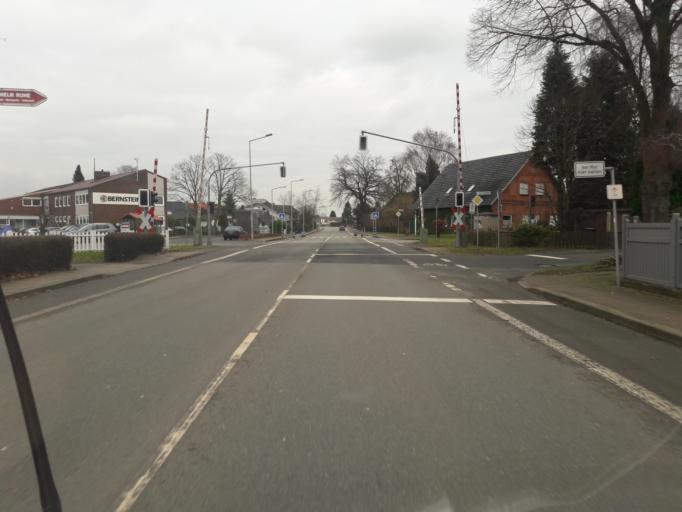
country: DE
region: North Rhine-Westphalia
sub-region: Regierungsbezirk Detmold
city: Hille
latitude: 52.3162
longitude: 8.8244
